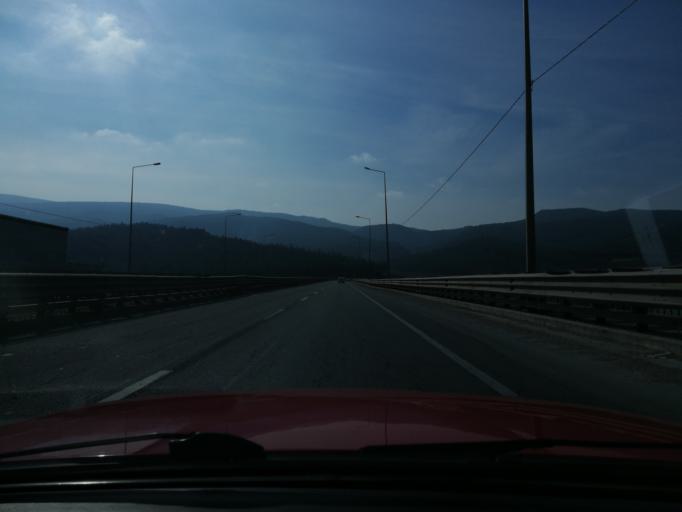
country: TR
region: Bilecik
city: Osmaneli
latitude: 40.4370
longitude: 30.0498
